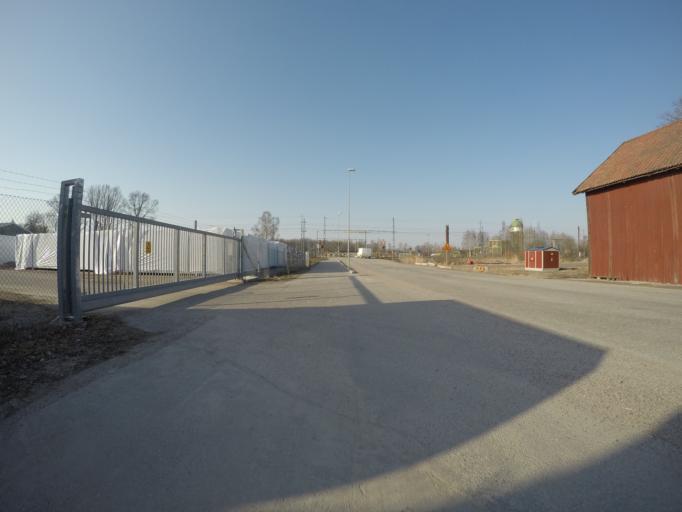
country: SE
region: Vaestmanland
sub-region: Kungsors Kommun
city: Kungsoer
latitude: 59.4275
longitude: 16.1121
